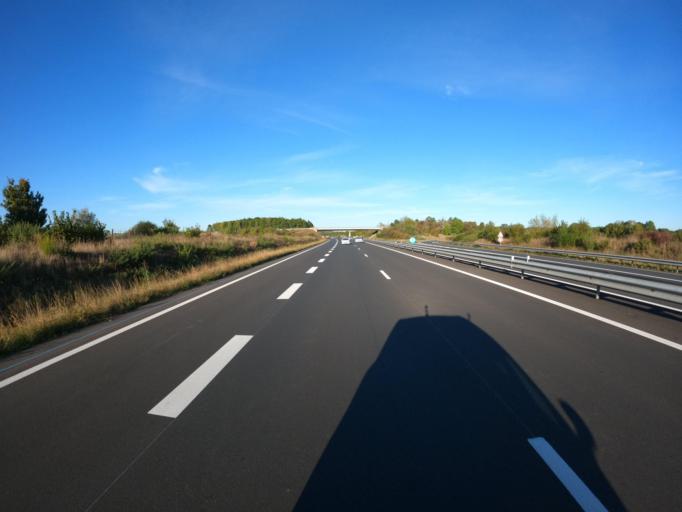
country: FR
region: Pays de la Loire
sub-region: Departement de la Vendee
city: Beaurepaire
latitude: 46.9021
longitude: -1.0566
